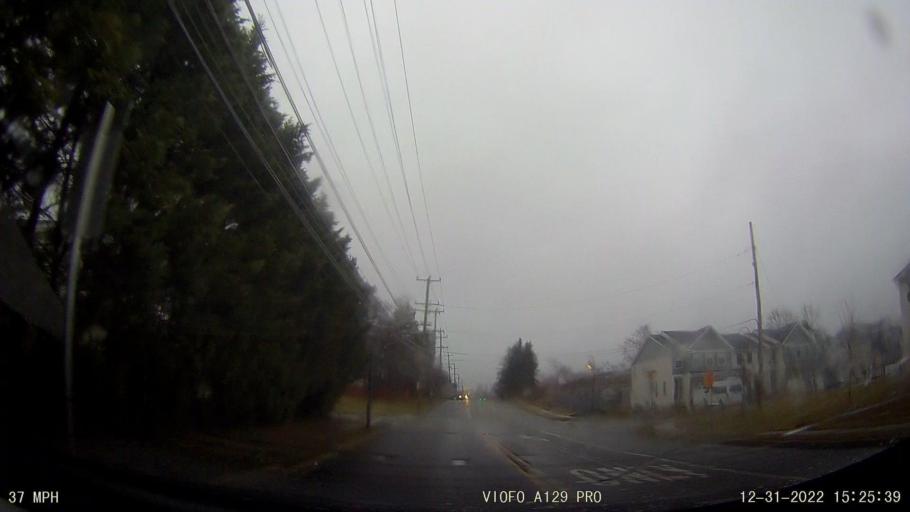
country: US
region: Pennsylvania
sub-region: Montgomery County
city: Bridgeport
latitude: 40.0977
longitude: -75.3665
